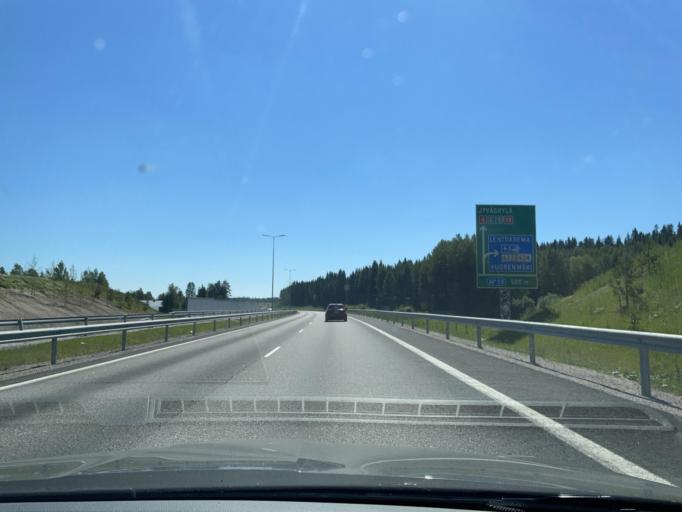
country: FI
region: Central Finland
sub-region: Jyvaeskylae
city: Jyvaeskylae
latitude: 62.4182
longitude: 25.6933
